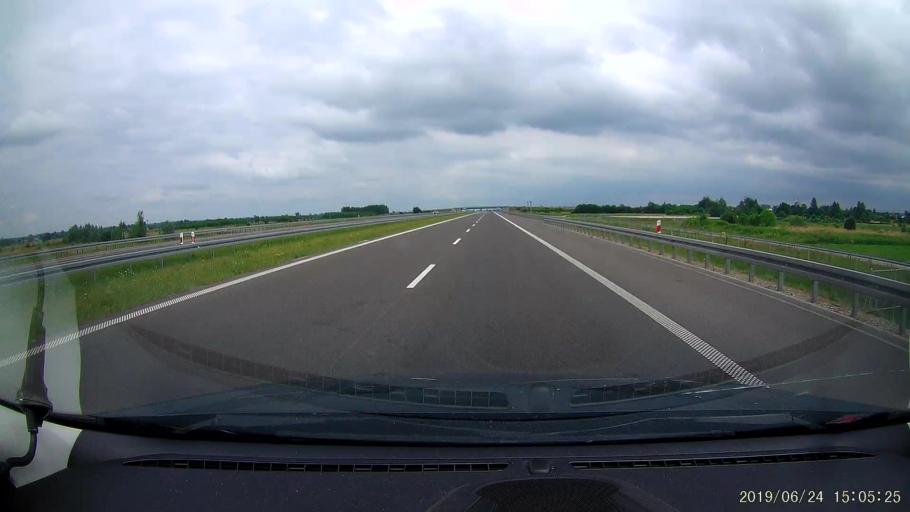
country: PL
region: Subcarpathian Voivodeship
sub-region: Powiat rzeszowski
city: Wolka Podlesna
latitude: 50.0930
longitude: 22.0892
